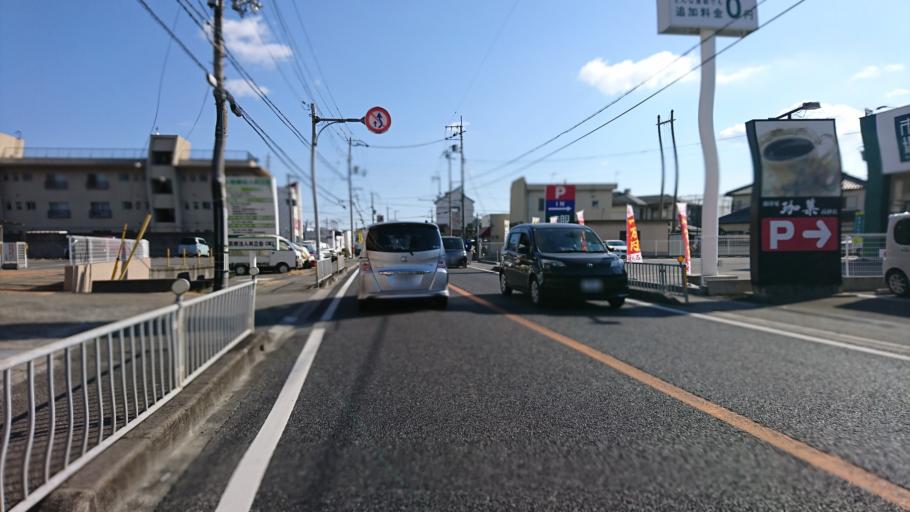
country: JP
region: Hyogo
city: Kakogawacho-honmachi
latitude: 34.7813
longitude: 134.8163
